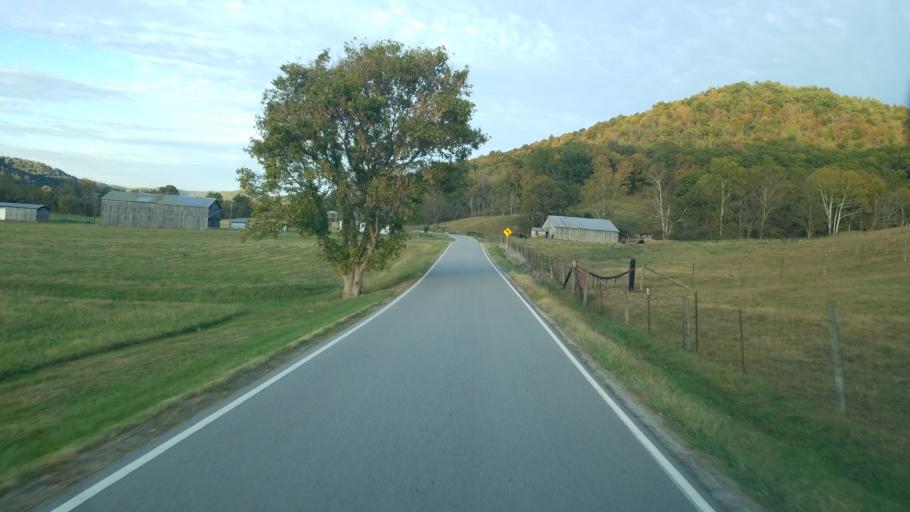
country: US
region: Kentucky
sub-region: Lewis County
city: Vanceburg
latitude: 38.5589
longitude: -83.4394
